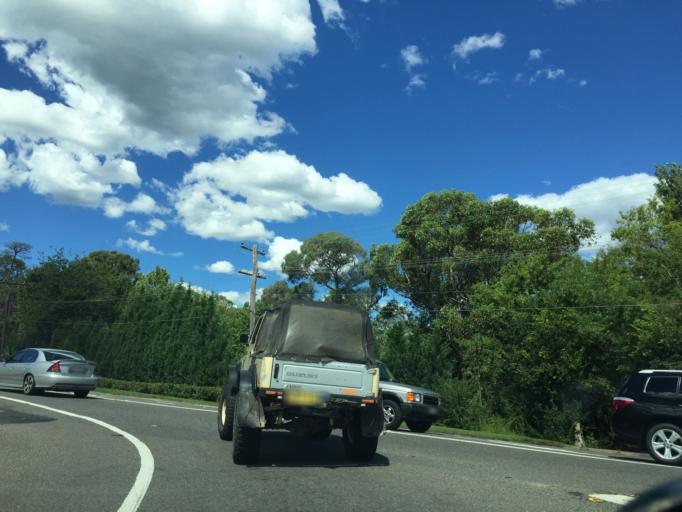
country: AU
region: New South Wales
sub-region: The Hills Shire
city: Glenhaven
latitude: -33.7058
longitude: 151.0116
